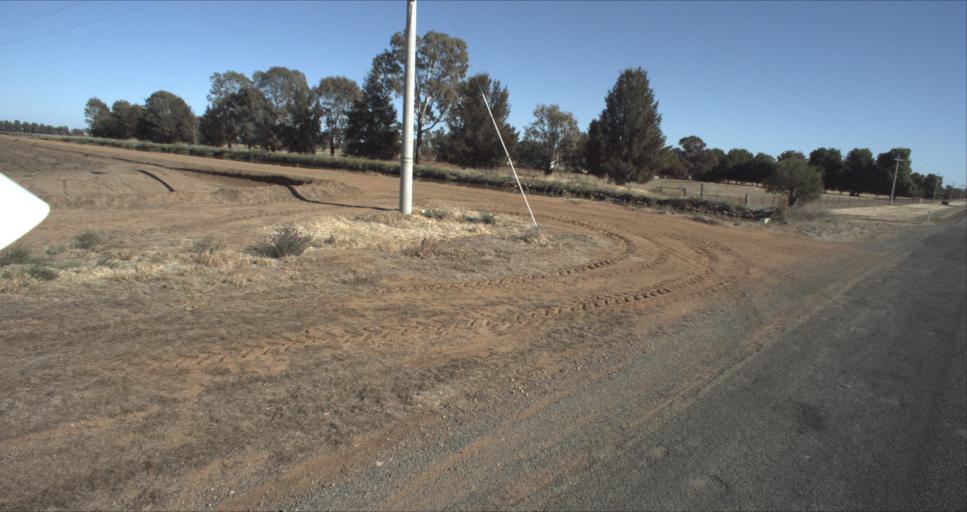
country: AU
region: New South Wales
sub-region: Leeton
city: Leeton
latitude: -34.5884
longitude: 146.2602
